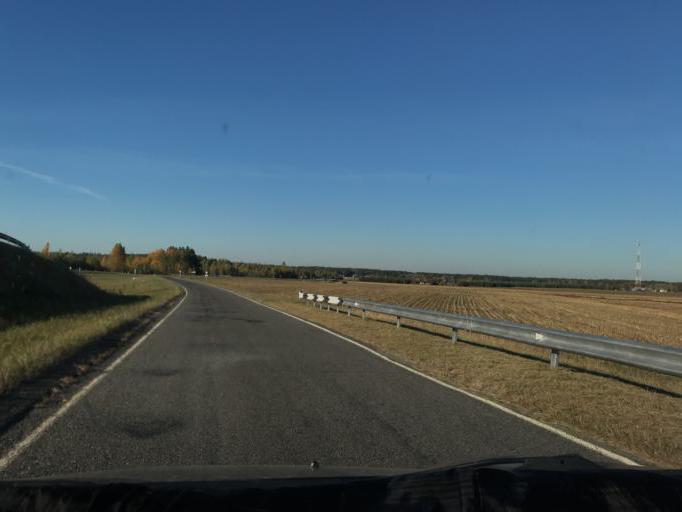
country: BY
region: Gomel
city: Kalinkavichy
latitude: 52.0732
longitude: 29.3634
